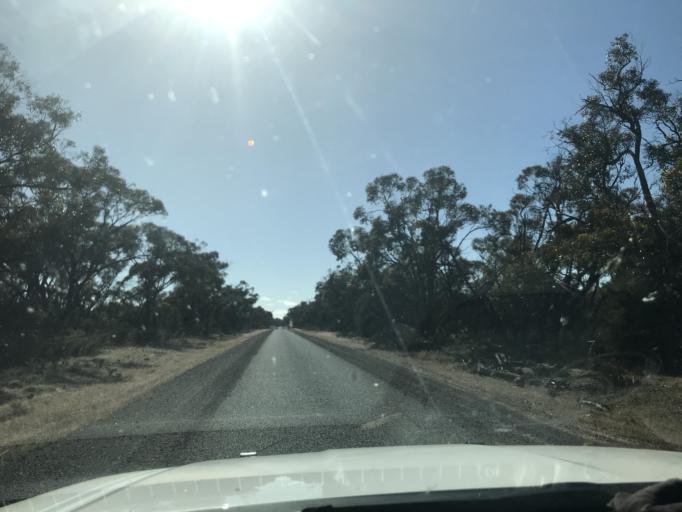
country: AU
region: Victoria
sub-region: Horsham
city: Horsham
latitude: -37.0231
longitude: 141.6849
